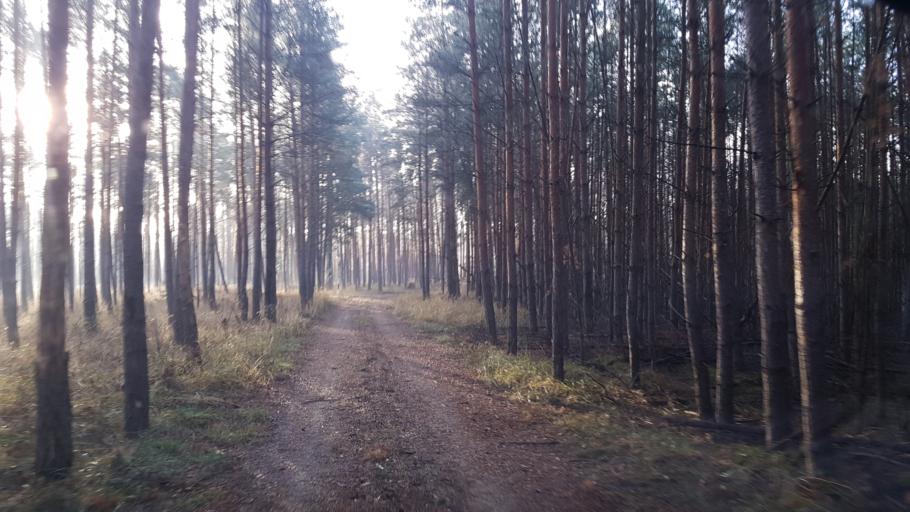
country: DE
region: Brandenburg
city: Schonborn
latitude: 51.5819
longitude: 13.4705
